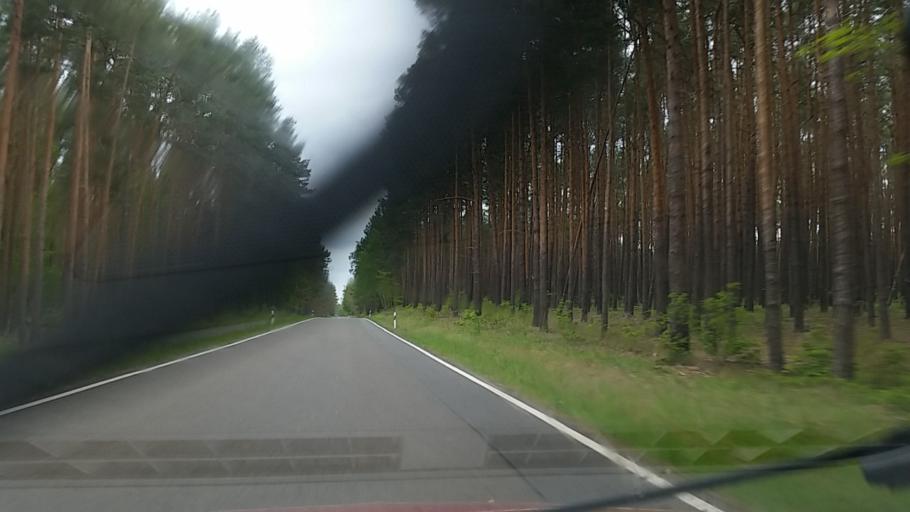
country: DE
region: Brandenburg
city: Reichenwalde
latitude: 52.3022
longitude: 13.9786
